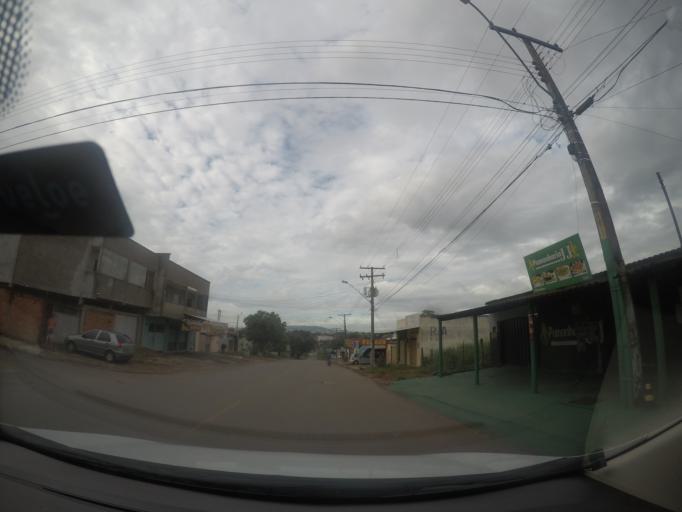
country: BR
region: Goias
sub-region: Goiania
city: Goiania
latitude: -16.6229
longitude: -49.3274
